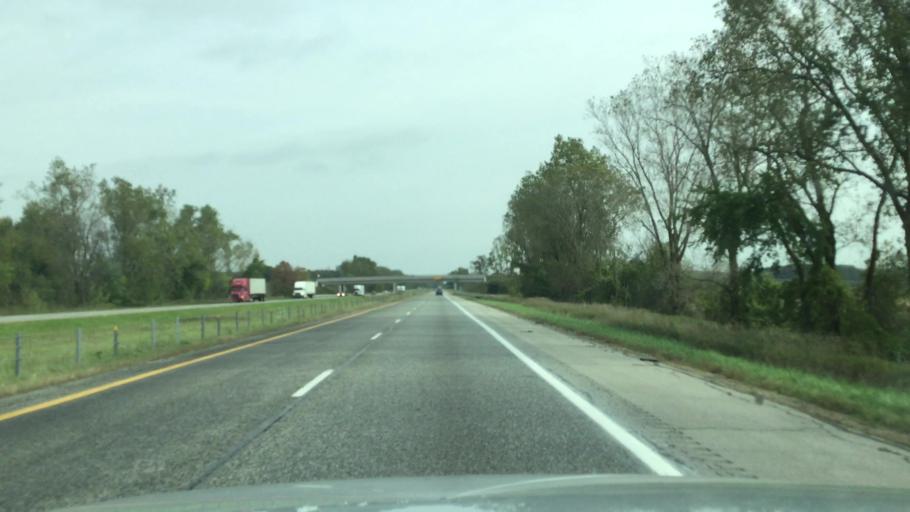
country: US
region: Michigan
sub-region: Shiawassee County
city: Corunna
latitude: 42.8765
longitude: -84.1256
